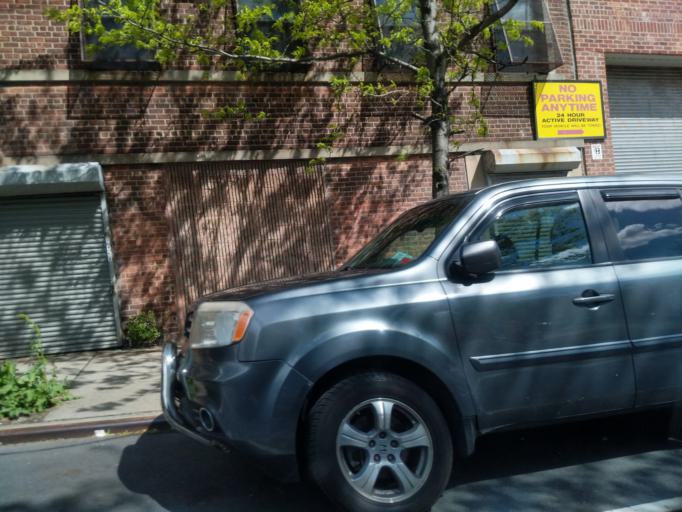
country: US
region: New York
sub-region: New York County
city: Inwood
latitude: 40.8222
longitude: -73.9280
